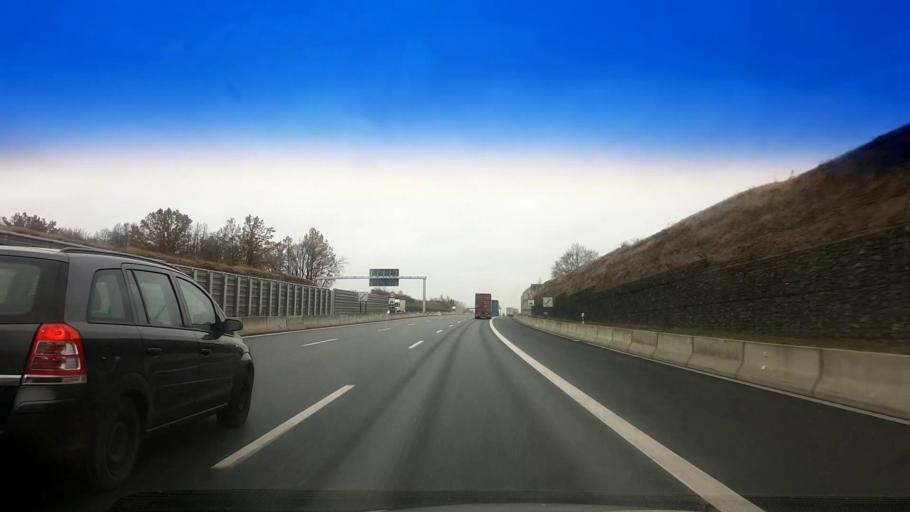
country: DE
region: Bavaria
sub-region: Upper Franconia
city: Bayreuth
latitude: 49.9518
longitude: 11.6076
